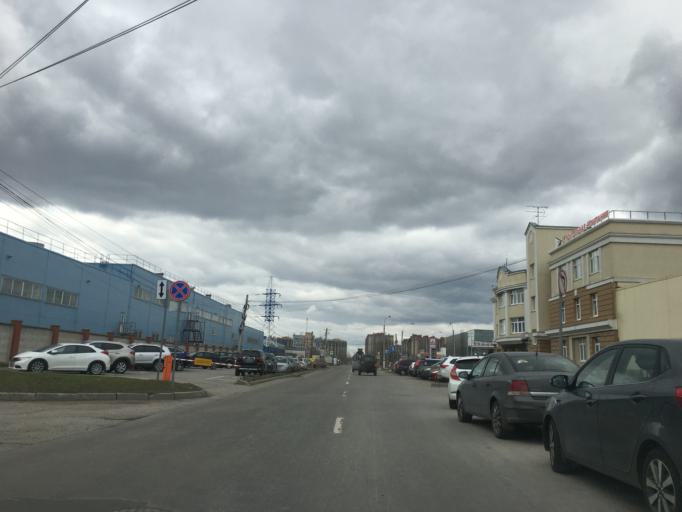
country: RU
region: Leningrad
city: Bugry
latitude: 60.0692
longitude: 30.3750
